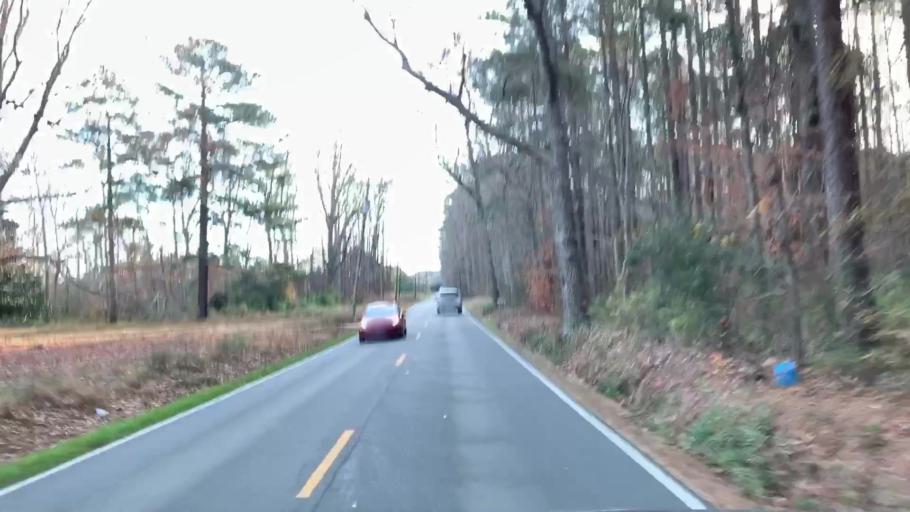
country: US
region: Virginia
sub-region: City of Virginia Beach
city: Virginia Beach
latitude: 36.7258
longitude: -76.0738
